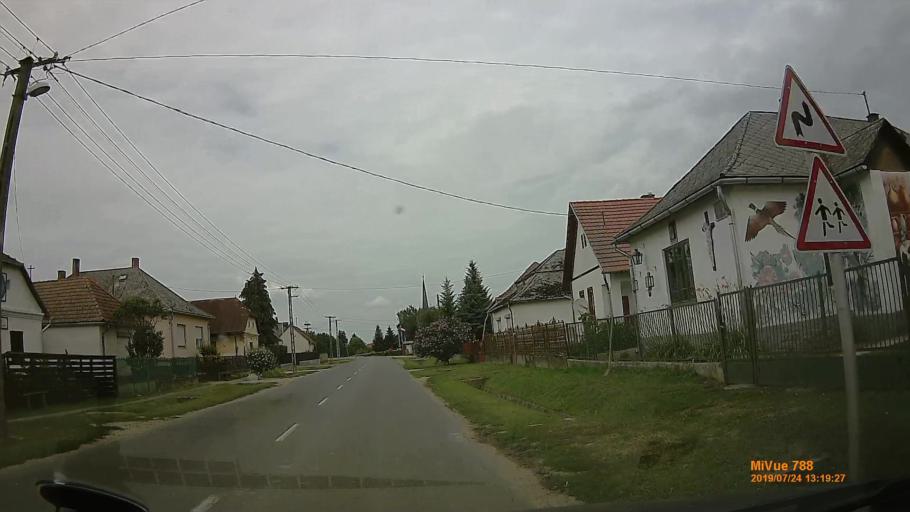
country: HU
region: Szabolcs-Szatmar-Bereg
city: Vasarosnameny
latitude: 48.1975
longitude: 22.4077
